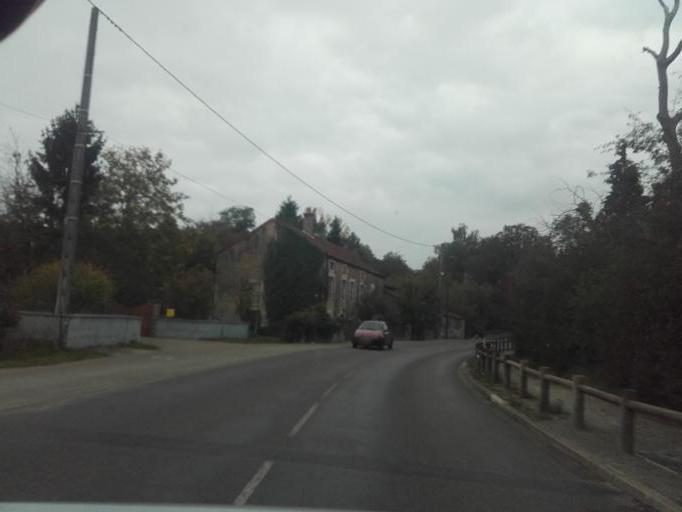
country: FR
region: Bourgogne
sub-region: Departement de Saone-et-Loire
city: Chagny
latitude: 46.9133
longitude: 4.7899
